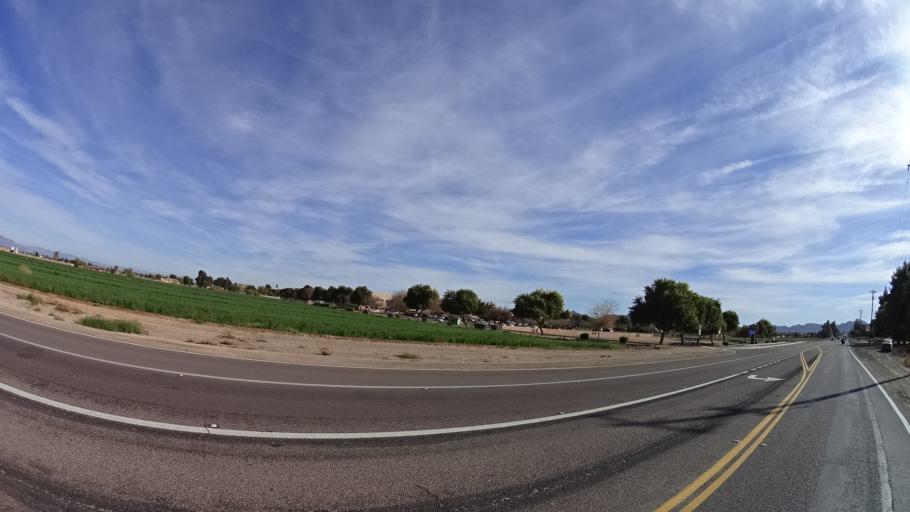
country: US
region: Arizona
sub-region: Maricopa County
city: Queen Creek
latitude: 33.2417
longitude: -111.6858
